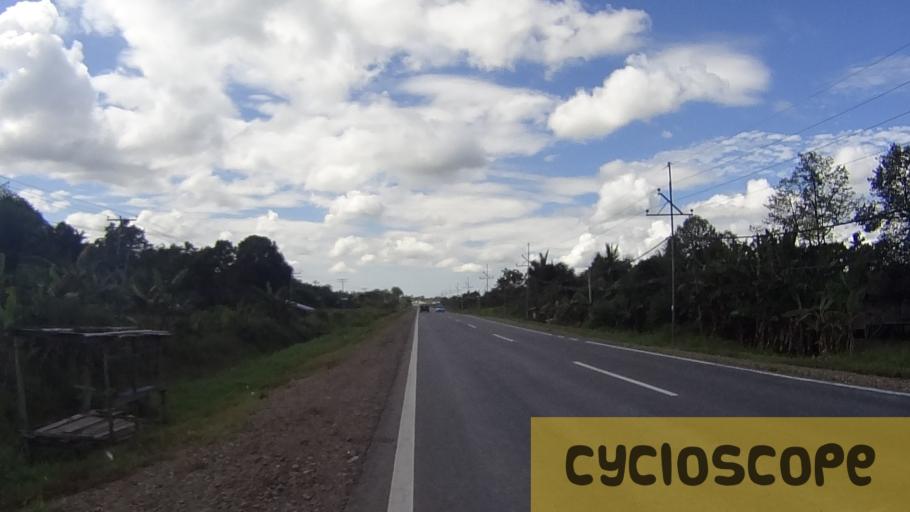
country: MY
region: Sabah
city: Beaufort
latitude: 5.2971
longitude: 115.6931
